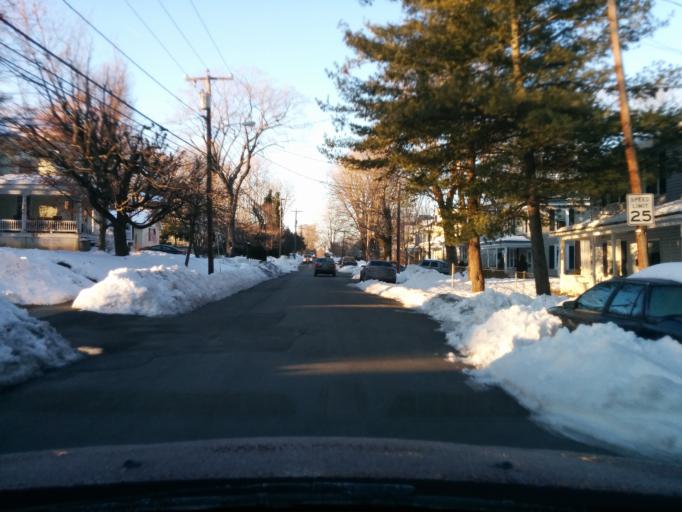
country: US
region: Virginia
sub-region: City of Lexington
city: Lexington
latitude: 37.7780
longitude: -79.4456
